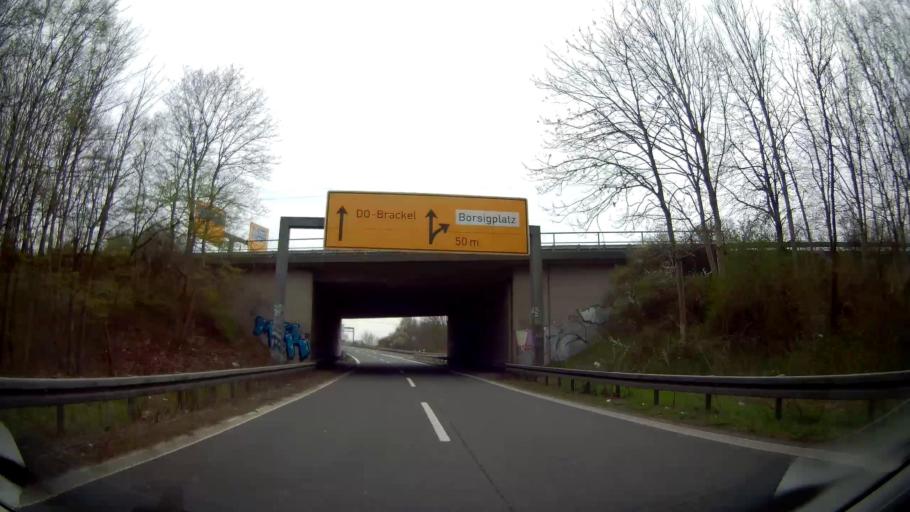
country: DE
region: North Rhine-Westphalia
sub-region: Regierungsbezirk Arnsberg
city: Dortmund
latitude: 51.5366
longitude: 7.5169
